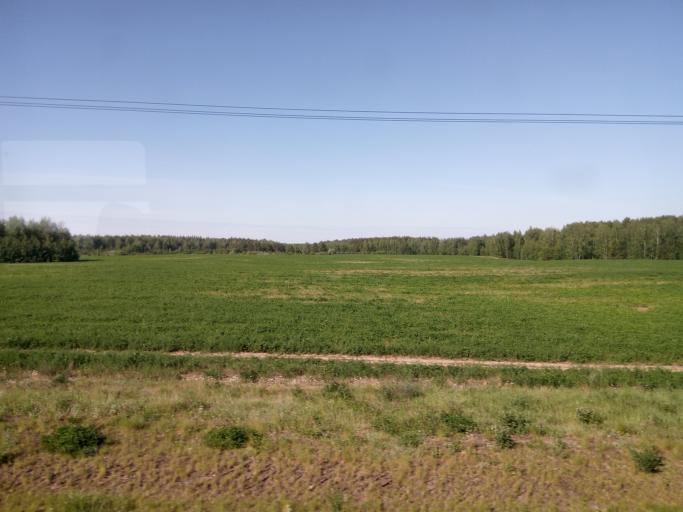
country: RU
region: Tatarstan
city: Stolbishchi
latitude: 55.6886
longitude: 49.1979
